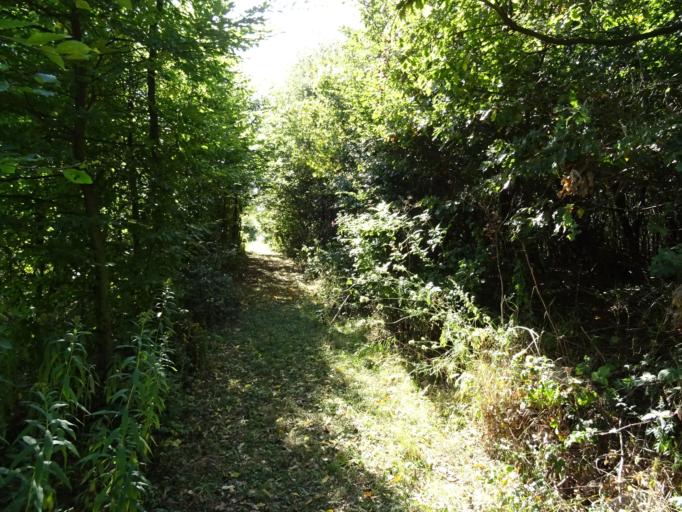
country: HU
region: Fejer
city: Bakonycsernye
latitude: 47.2768
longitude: 18.0847
